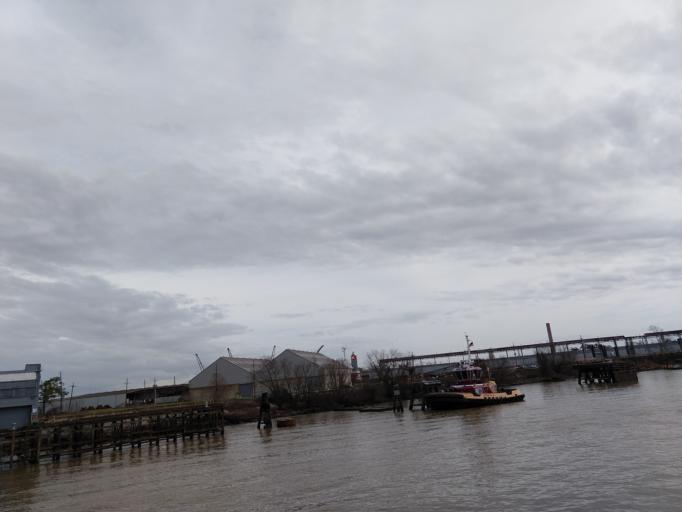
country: US
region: Louisiana
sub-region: Saint Bernard Parish
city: Arabi
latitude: 29.9424
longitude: -90.0009
